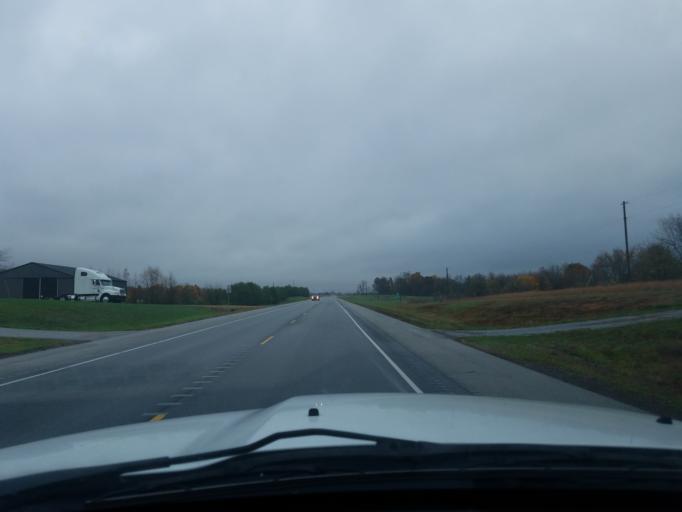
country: US
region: Kentucky
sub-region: Larue County
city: Hodgenville
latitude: 37.5187
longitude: -85.6450
